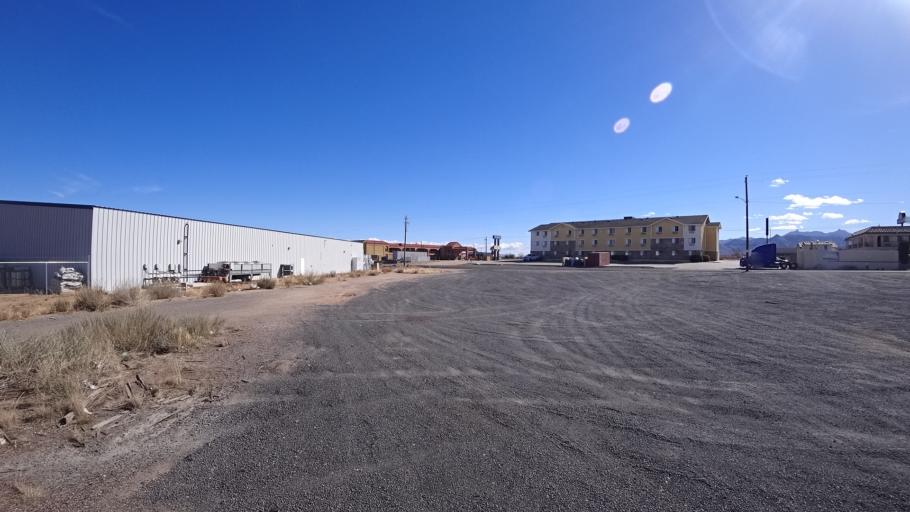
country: US
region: Arizona
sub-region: Mohave County
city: New Kingman-Butler
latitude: 35.2235
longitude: -114.0068
